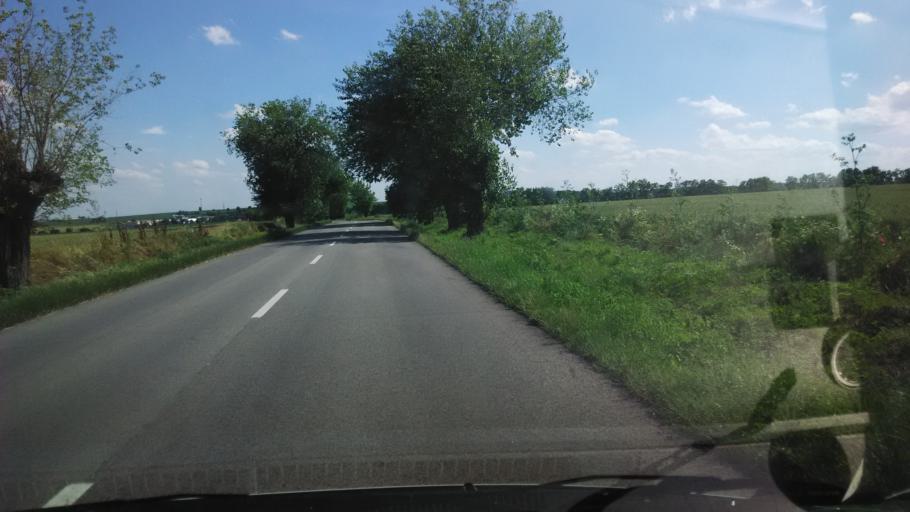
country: SK
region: Nitriansky
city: Tlmace
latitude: 48.1698
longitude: 18.4516
